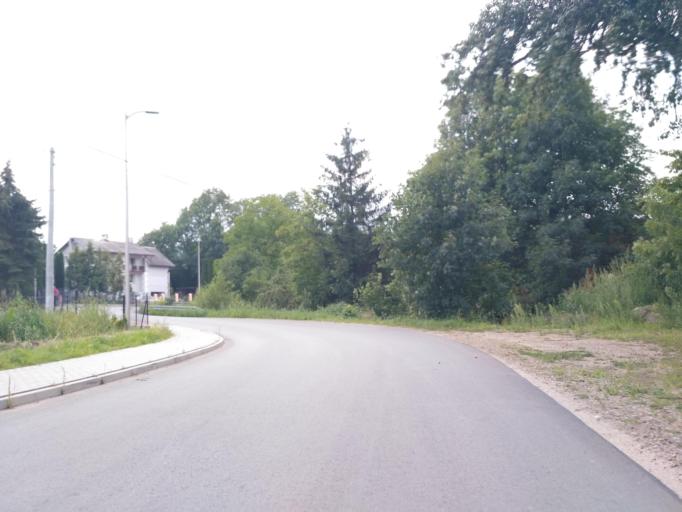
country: PL
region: Subcarpathian Voivodeship
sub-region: Powiat krosnienski
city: Iwonicz-Zdroj
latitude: 49.5745
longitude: 21.8194
